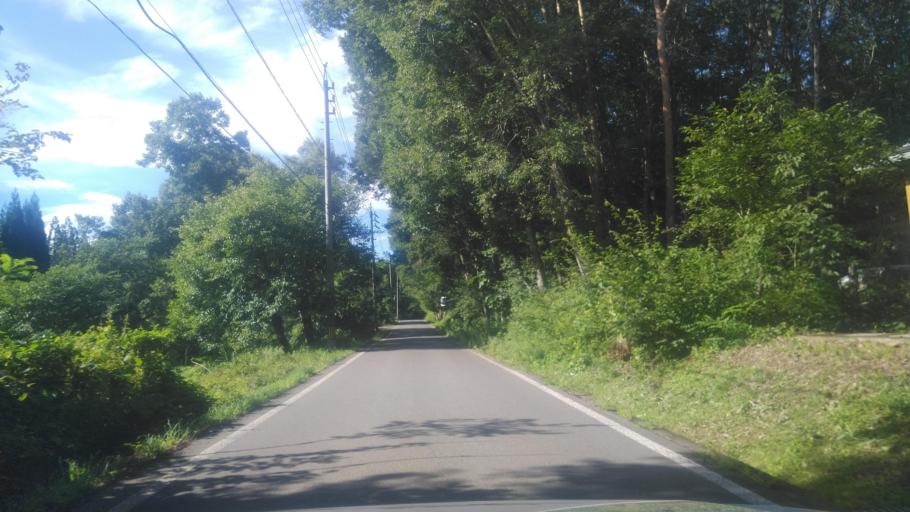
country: JP
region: Nagano
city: Nagano-shi
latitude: 36.7899
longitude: 138.1784
